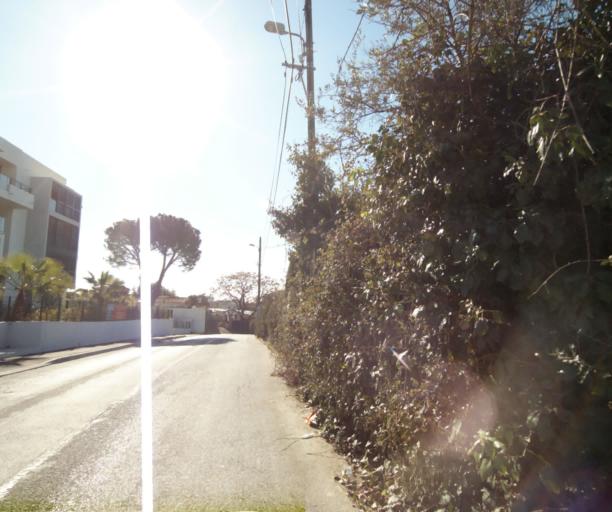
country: FR
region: Provence-Alpes-Cote d'Azur
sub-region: Departement des Alpes-Maritimes
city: Biot
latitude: 43.5983
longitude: 7.1054
